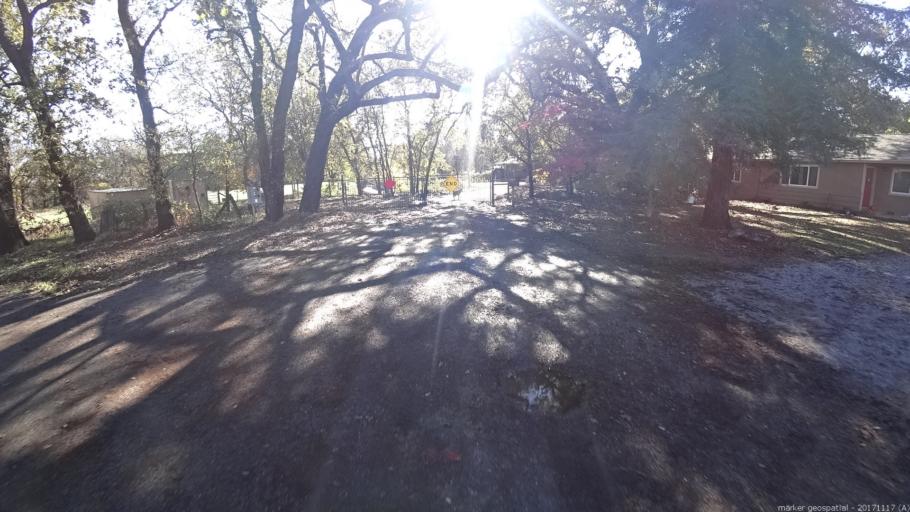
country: US
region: California
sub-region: Shasta County
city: Cottonwood
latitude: 40.4262
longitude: -122.2167
